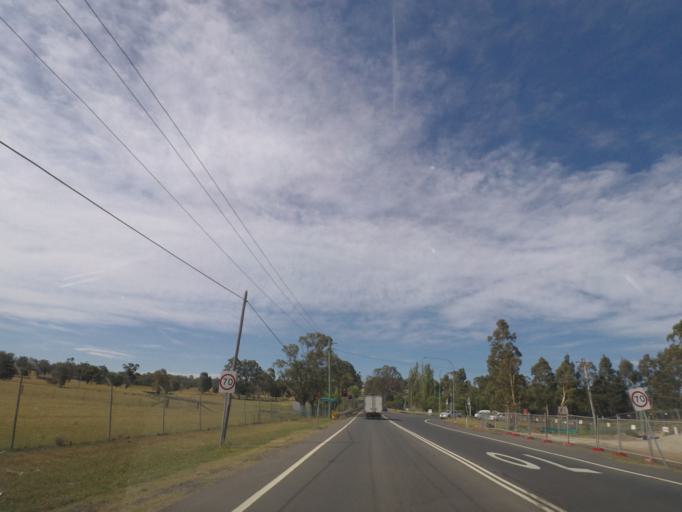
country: AU
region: New South Wales
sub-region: Campbelltown Municipality
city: Denham Court
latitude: -33.9989
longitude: 150.8415
